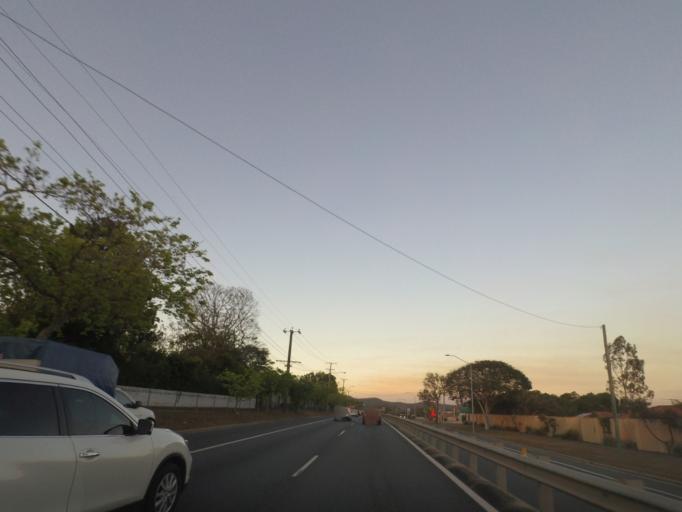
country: AU
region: Queensland
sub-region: Brisbane
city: Mansfield
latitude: -27.5511
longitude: 153.1051
